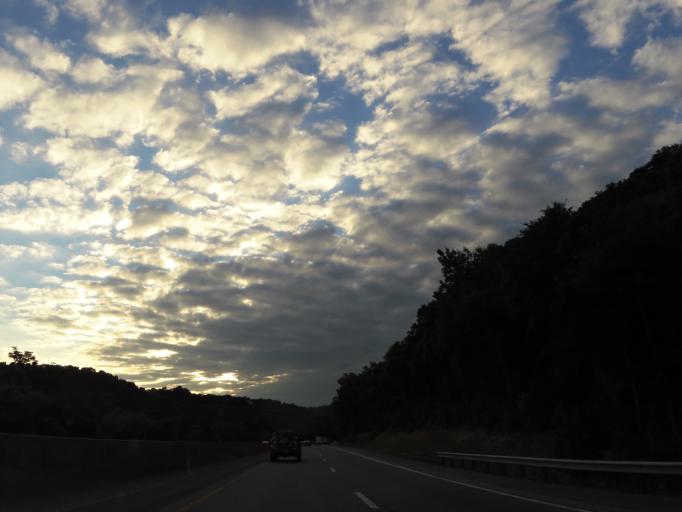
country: US
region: Tennessee
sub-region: Putnam County
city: Lafayette
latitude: 36.1062
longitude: -85.7653
